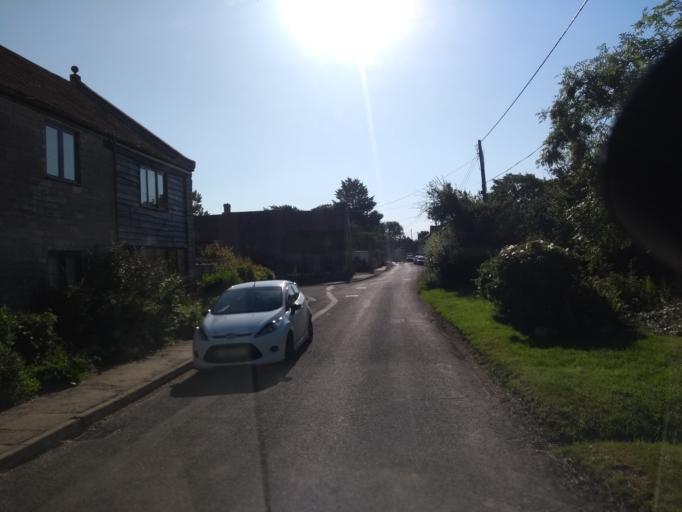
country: GB
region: England
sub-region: Somerset
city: Westonzoyland
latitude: 51.1405
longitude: -2.9071
